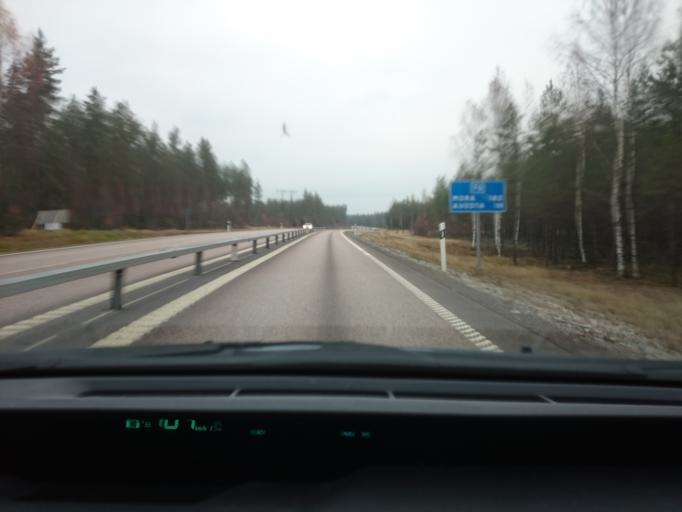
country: SE
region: Dalarna
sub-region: Avesta Kommun
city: Avesta
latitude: 60.0397
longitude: 16.3418
